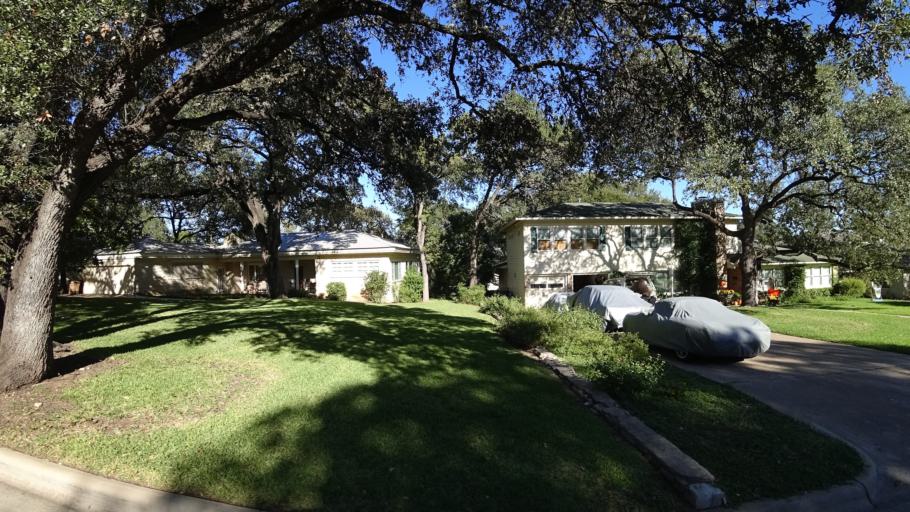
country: US
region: Texas
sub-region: Travis County
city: West Lake Hills
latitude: 30.3308
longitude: -97.7628
